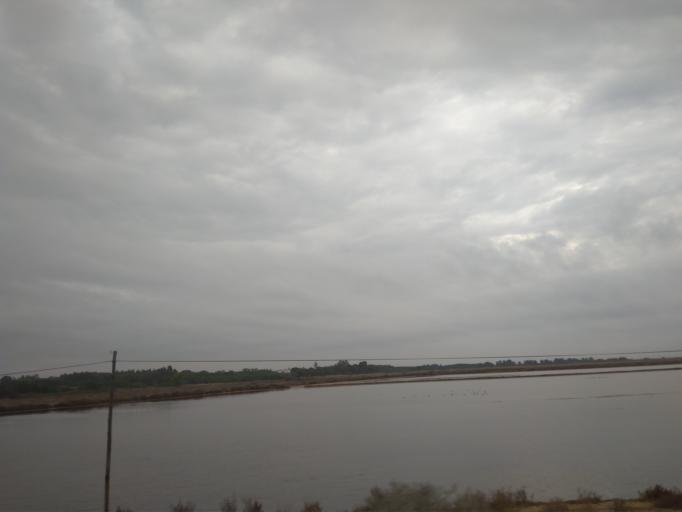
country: PT
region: Faro
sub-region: Faro
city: Faro
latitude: 37.0340
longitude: -7.9886
